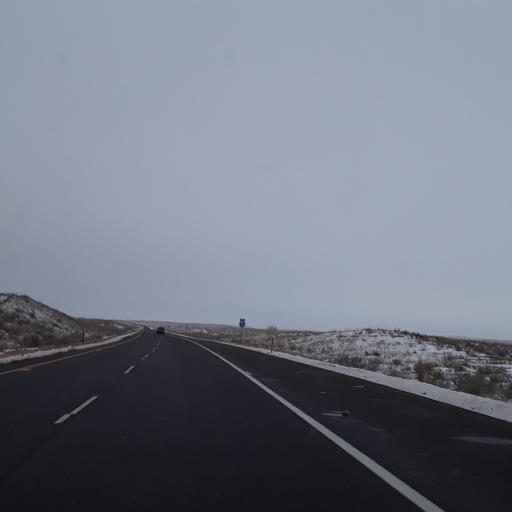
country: US
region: Colorado
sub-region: Logan County
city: Sterling
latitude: 40.6276
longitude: -103.1656
